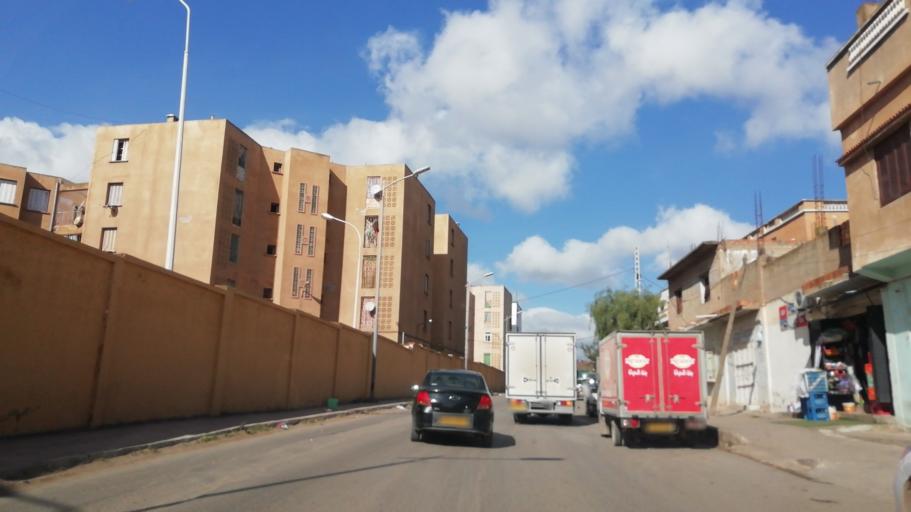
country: DZ
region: Oran
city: Es Senia
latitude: 35.6419
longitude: -0.6701
